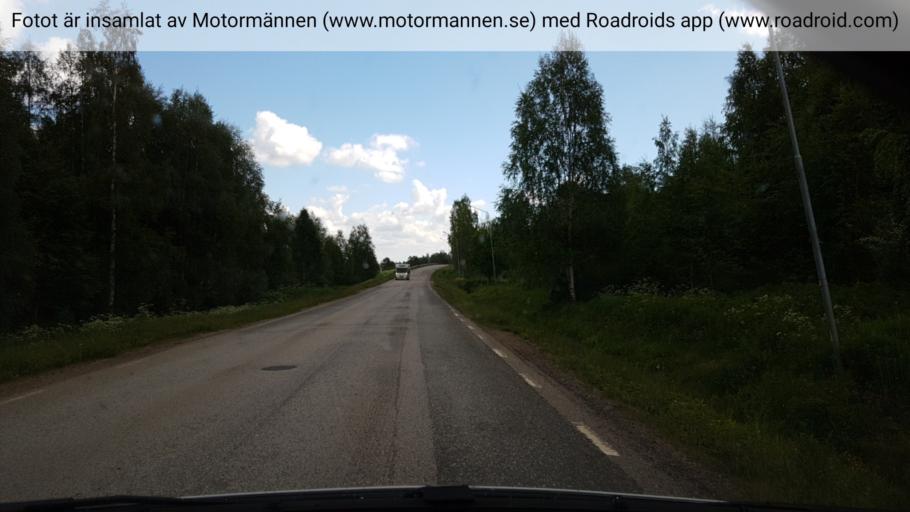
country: FI
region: Lapland
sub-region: Torniolaakso
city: Ylitornio
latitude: 66.1857
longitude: 23.7600
